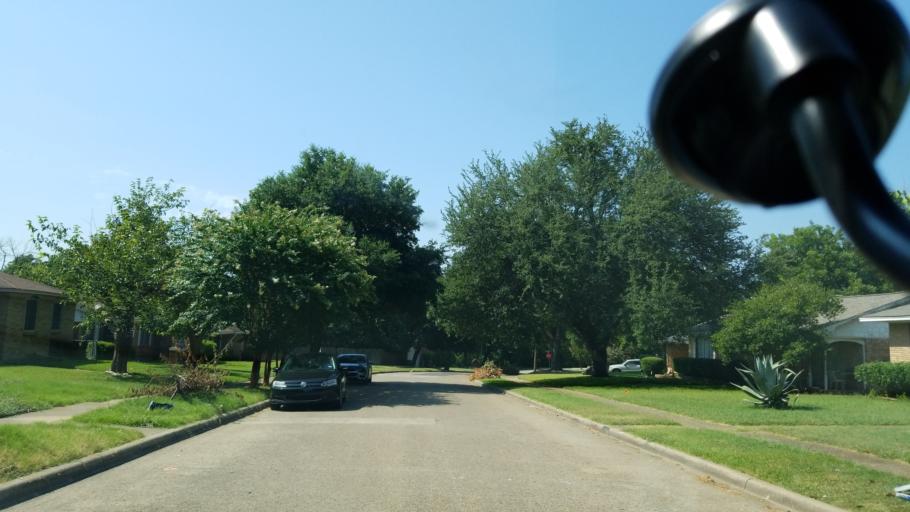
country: US
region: Texas
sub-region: Dallas County
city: Cockrell Hill
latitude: 32.7088
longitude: -96.8767
